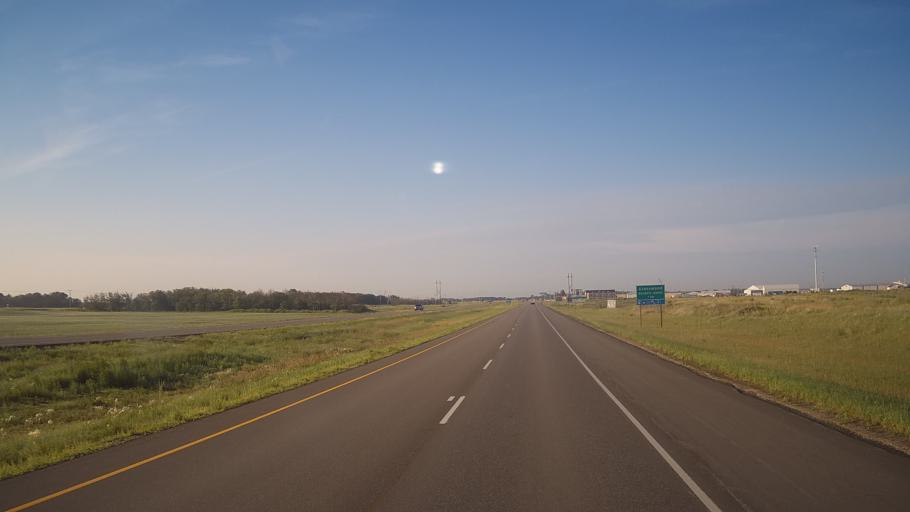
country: CA
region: Saskatchewan
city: Saskatoon
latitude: 52.0661
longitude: -106.6025
